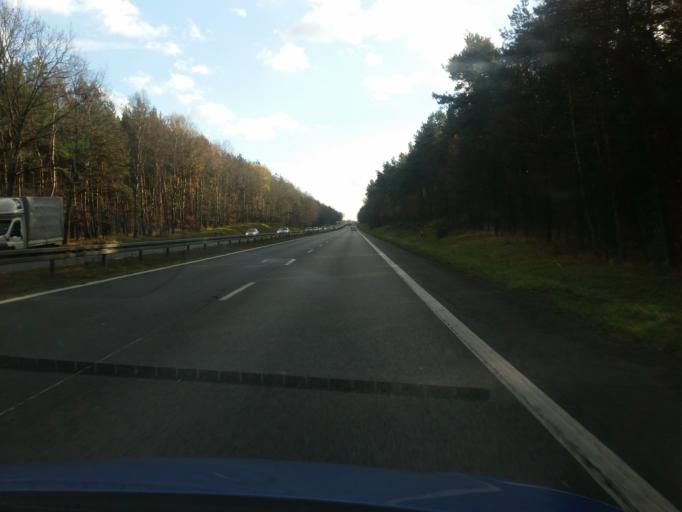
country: PL
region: Silesian Voivodeship
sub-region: Powiat czestochowski
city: Kamienica Polska
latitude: 50.6537
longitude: 19.1318
